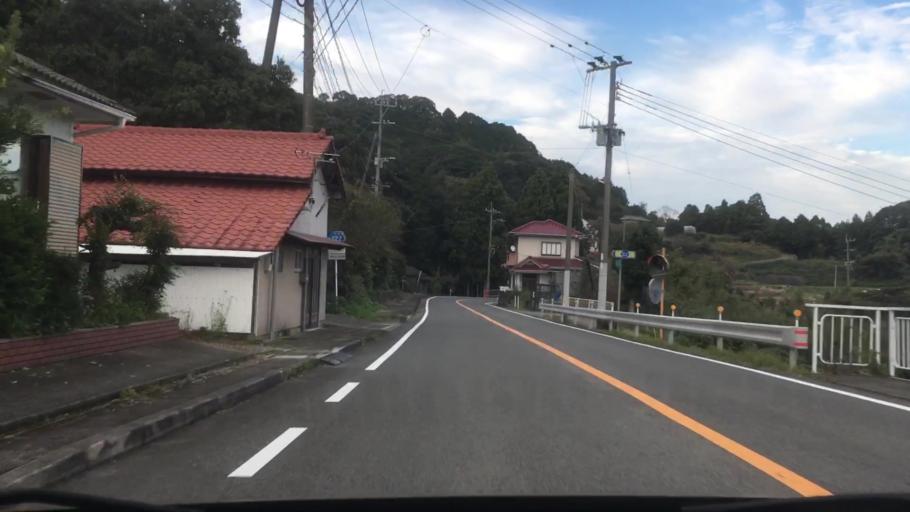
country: JP
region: Nagasaki
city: Sasebo
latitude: 32.9868
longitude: 129.7195
